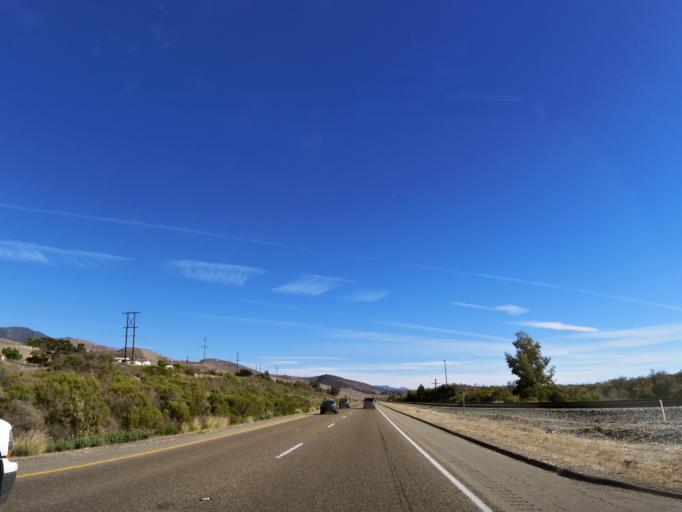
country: US
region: California
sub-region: Santa Barbara County
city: Santa Ynez
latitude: 34.4626
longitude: -120.0522
